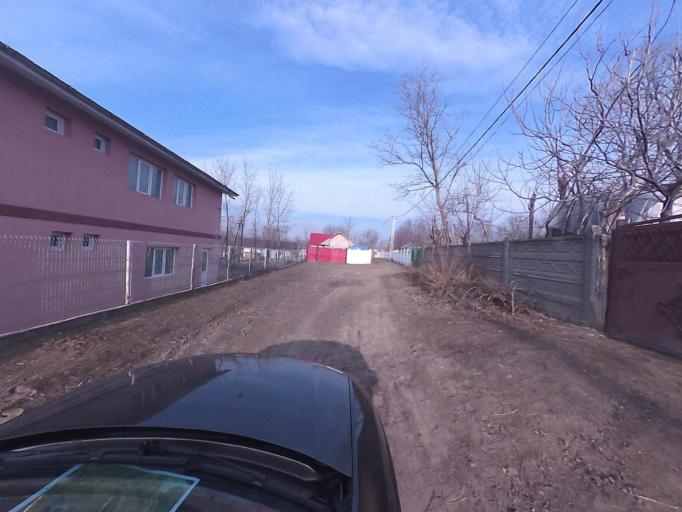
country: RO
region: Vaslui
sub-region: Comuna Solesti
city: Solesti
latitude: 46.8116
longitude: 27.7735
